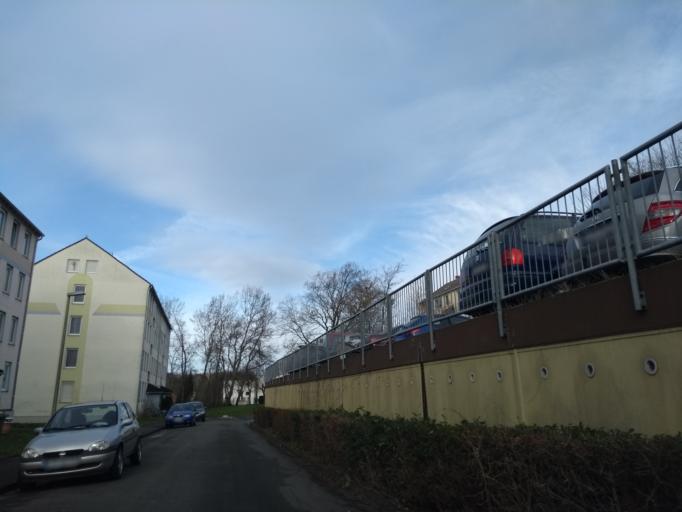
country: DE
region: North Rhine-Westphalia
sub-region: Regierungsbezirk Detmold
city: Detmold
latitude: 51.9504
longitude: 8.9014
